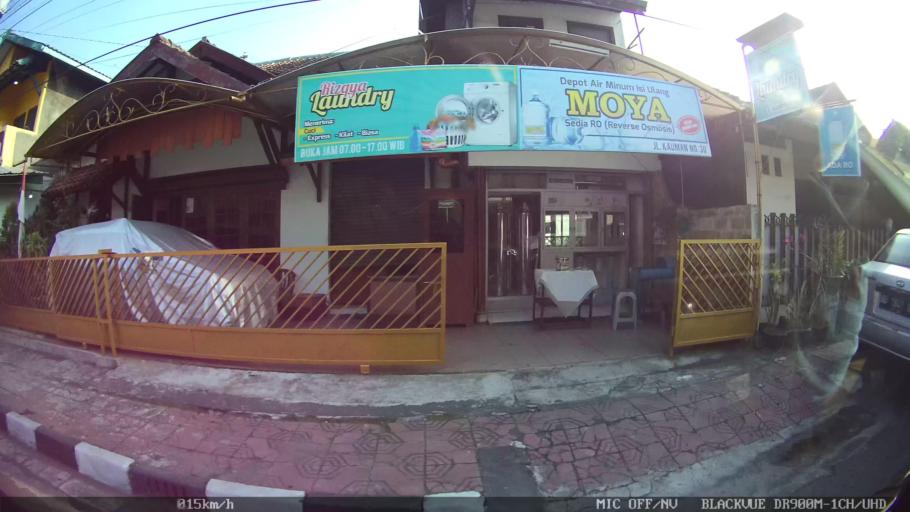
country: ID
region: Daerah Istimewa Yogyakarta
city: Yogyakarta
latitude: -7.8045
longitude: 110.3617
